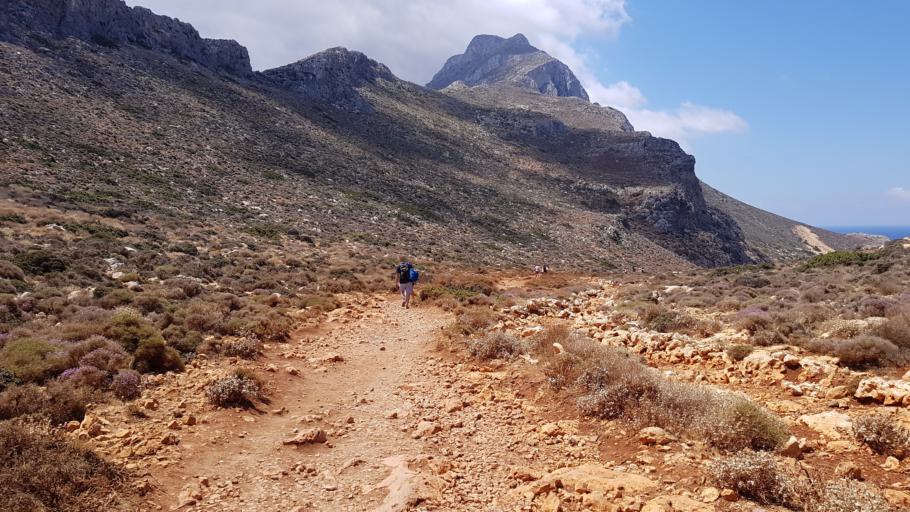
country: GR
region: Crete
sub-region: Nomos Chanias
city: Kissamos
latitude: 35.5855
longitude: 23.5963
